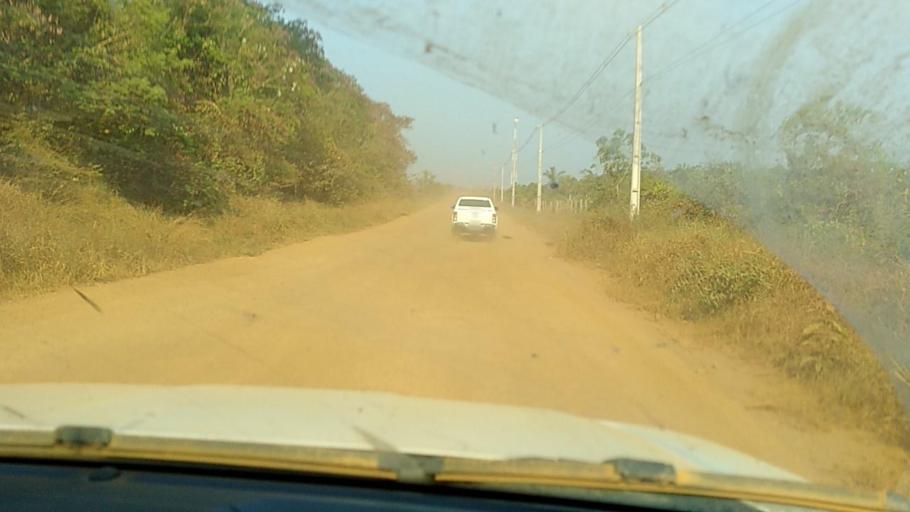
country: BR
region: Rondonia
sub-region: Porto Velho
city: Porto Velho
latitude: -8.7600
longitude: -63.9654
